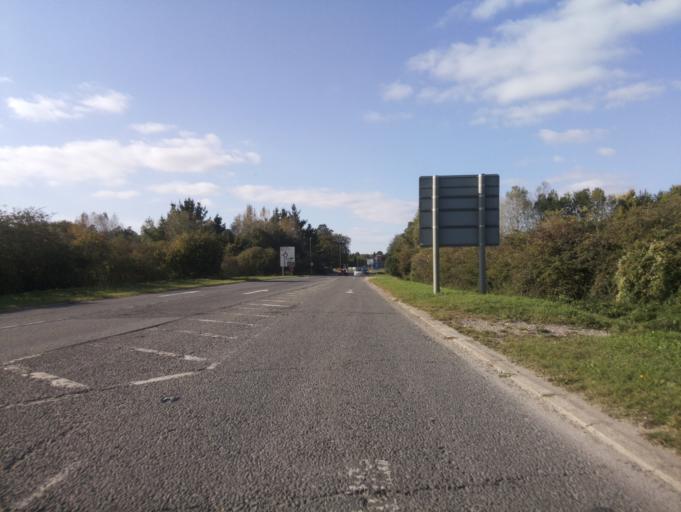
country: GB
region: England
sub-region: Hampshire
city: Alton
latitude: 51.1382
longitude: -0.9814
